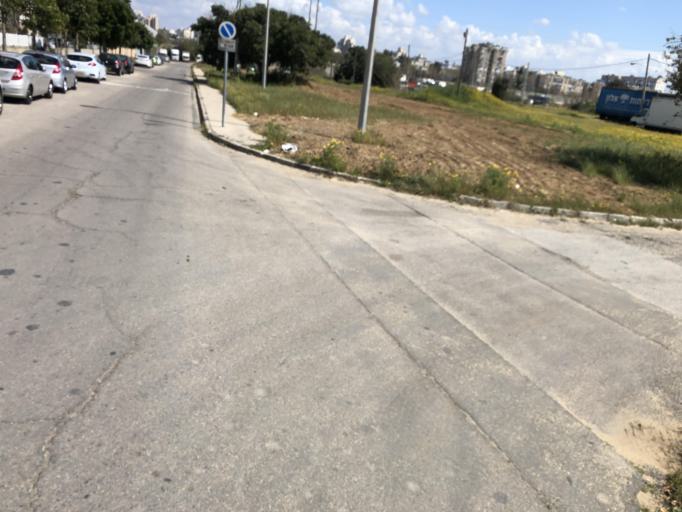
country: IL
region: Tel Aviv
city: Bat Yam
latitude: 32.0065
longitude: 34.7583
